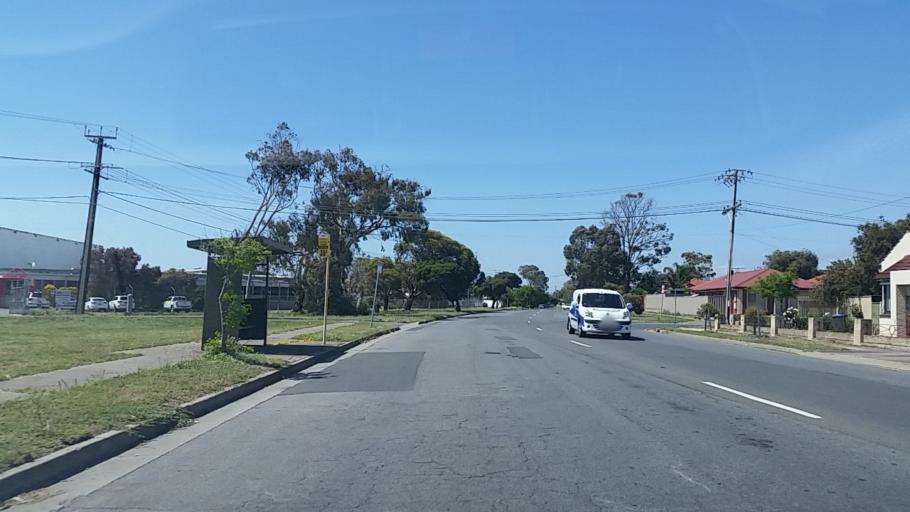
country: AU
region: South Australia
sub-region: Charles Sturt
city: West Lakes Shore
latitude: -34.8584
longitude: 138.5038
